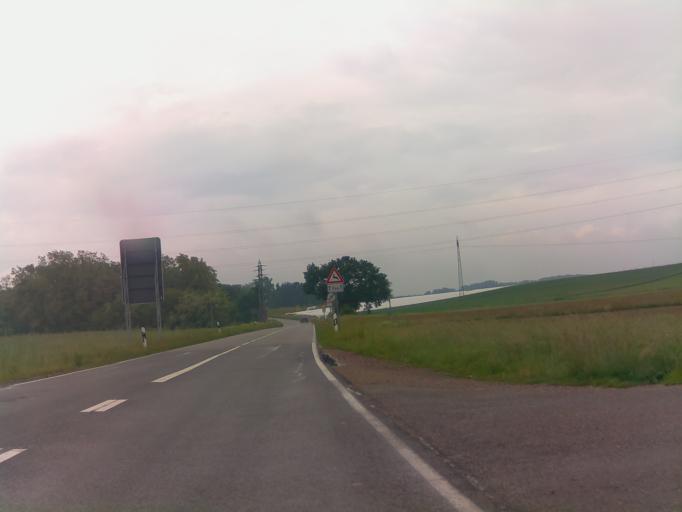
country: DE
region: Rheinland-Pfalz
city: Hordt
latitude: 49.1841
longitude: 8.3103
